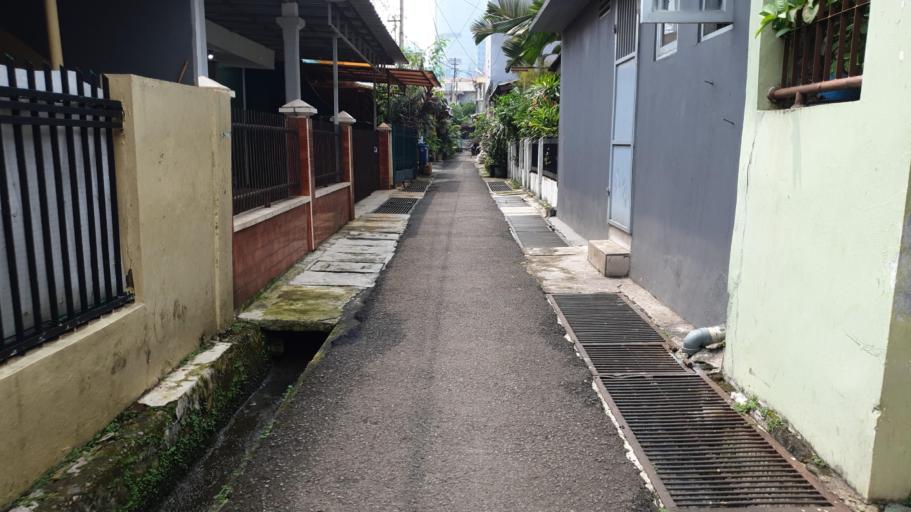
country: ID
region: Banten
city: South Tangerang
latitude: -6.2583
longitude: 106.7827
